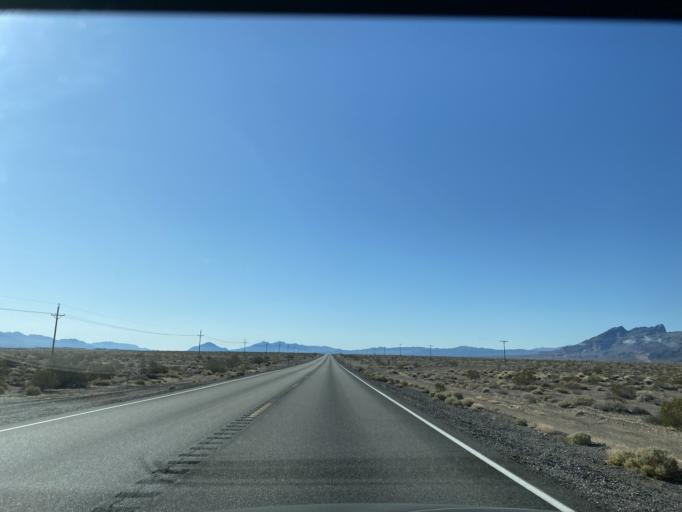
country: US
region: Nevada
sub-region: Nye County
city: Pahrump
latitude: 36.4547
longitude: -116.4218
